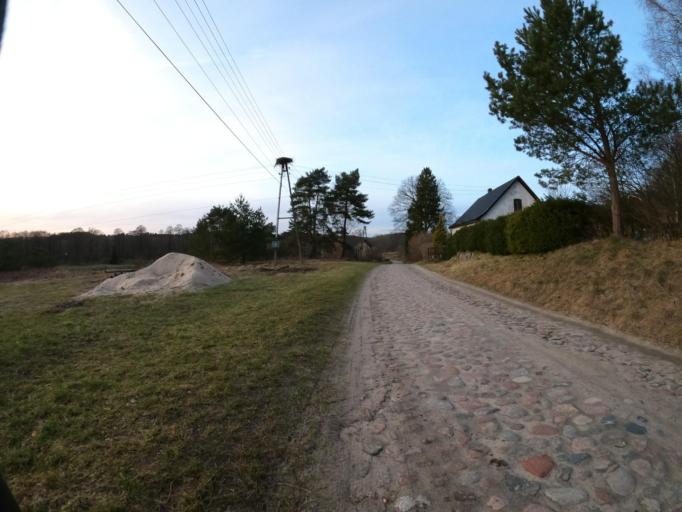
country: PL
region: West Pomeranian Voivodeship
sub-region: Powiat koszalinski
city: Polanow
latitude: 54.1994
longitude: 16.7158
